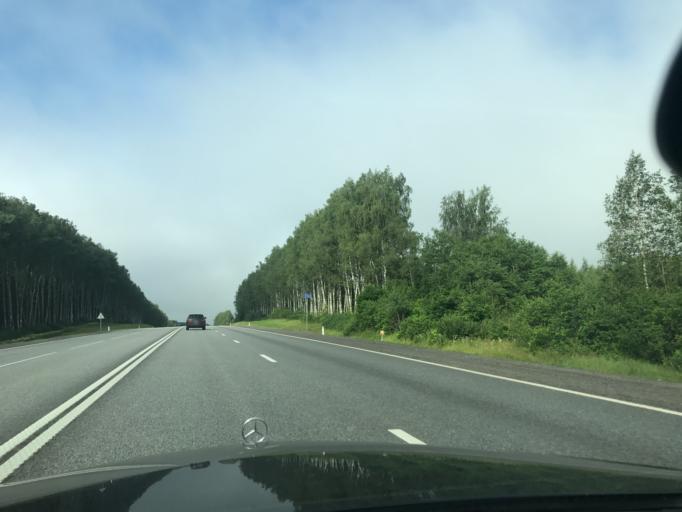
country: RU
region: Smolensk
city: Vyaz'ma
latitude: 55.2988
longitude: 34.4855
